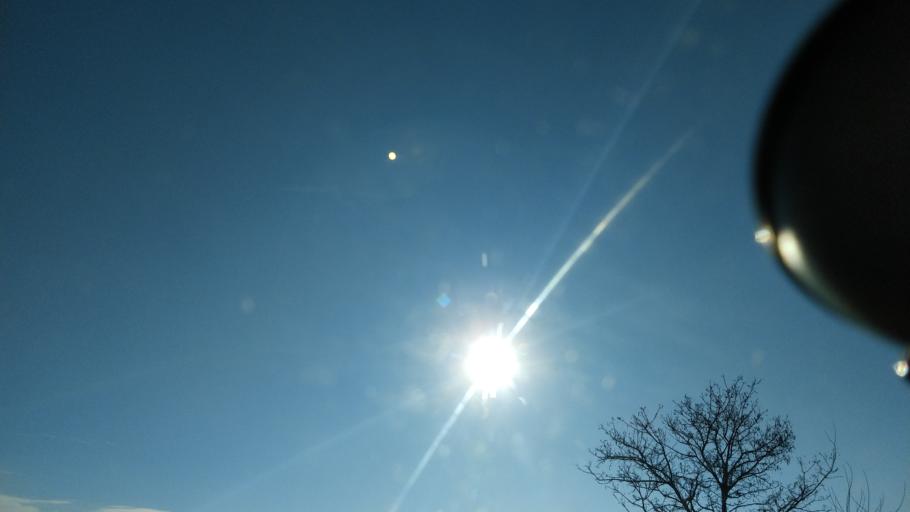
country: RO
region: Iasi
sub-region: Comuna Butea
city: Butea
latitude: 47.0809
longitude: 26.8994
